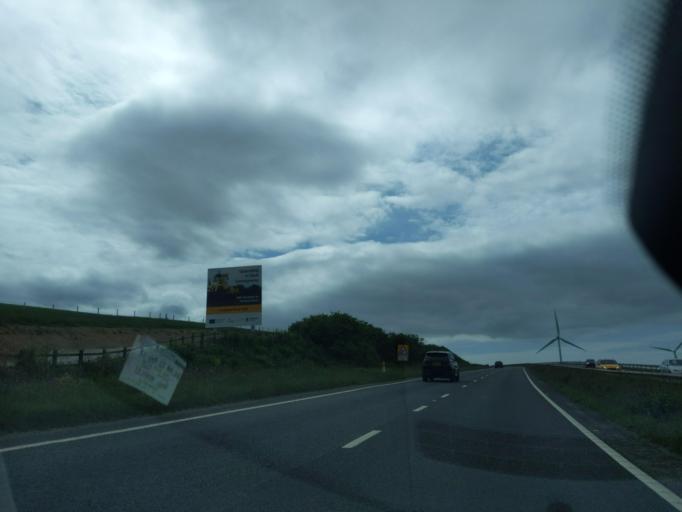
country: GB
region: England
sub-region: Cornwall
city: Probus
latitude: 50.3503
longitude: -5.0172
